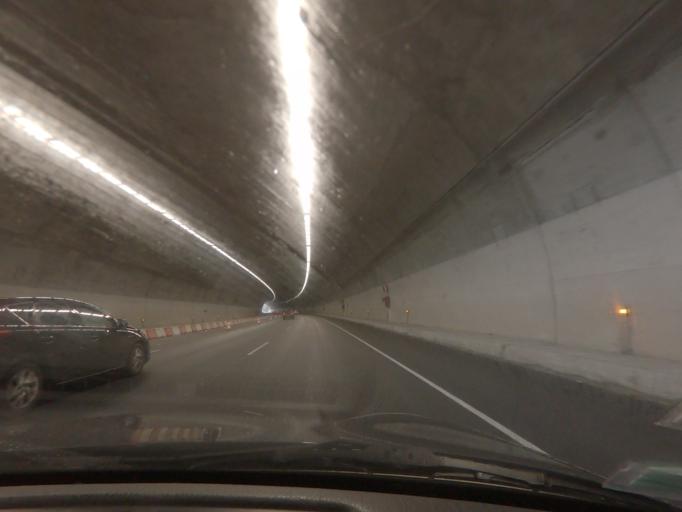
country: PT
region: Porto
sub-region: Maia
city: Pedroucos
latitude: 41.1993
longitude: -8.5752
